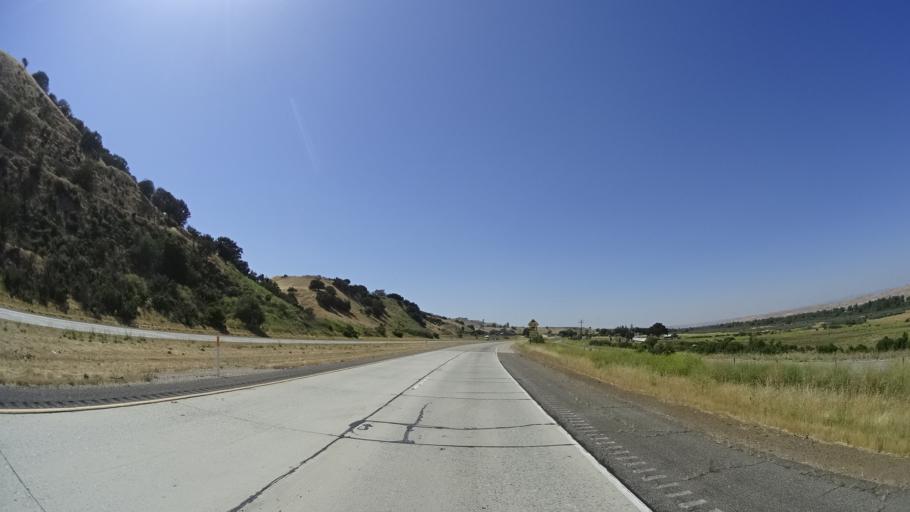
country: US
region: California
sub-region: San Luis Obispo County
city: Lake Nacimiento
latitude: 35.9686
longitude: -120.8938
